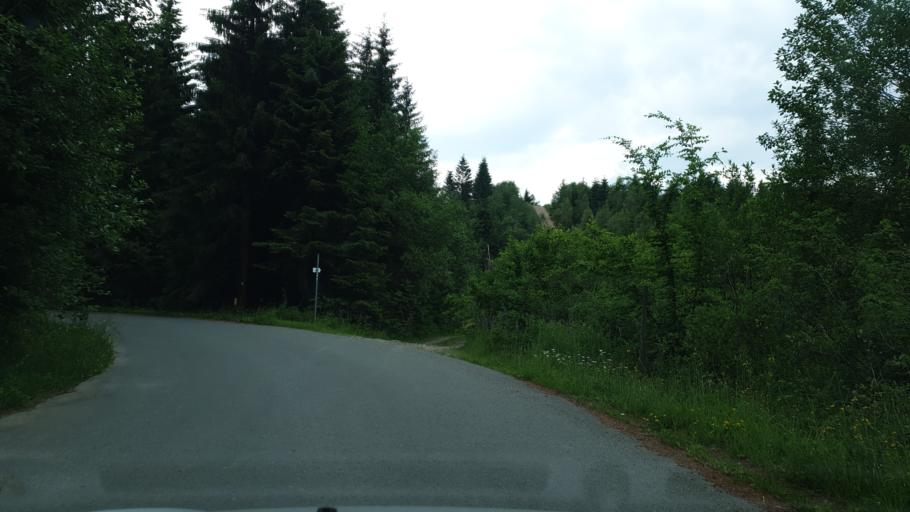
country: DE
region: Saxony
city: Tannenbergsthal
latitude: 50.4096
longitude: 12.4436
